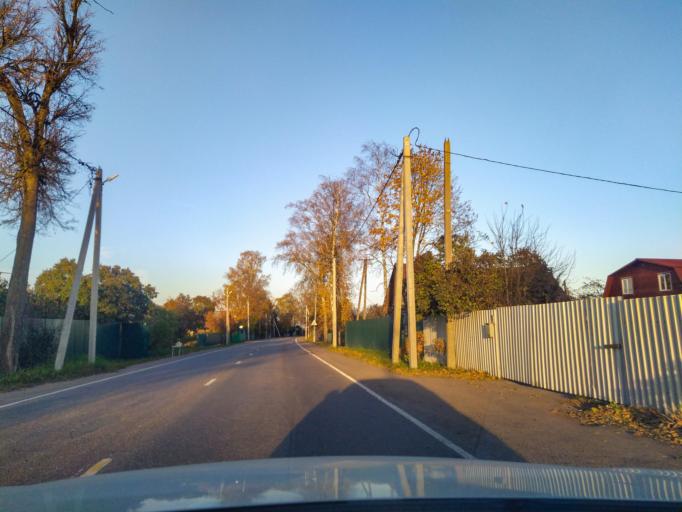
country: RU
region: Leningrad
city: Kobrinskoye
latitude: 59.4752
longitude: 30.1272
